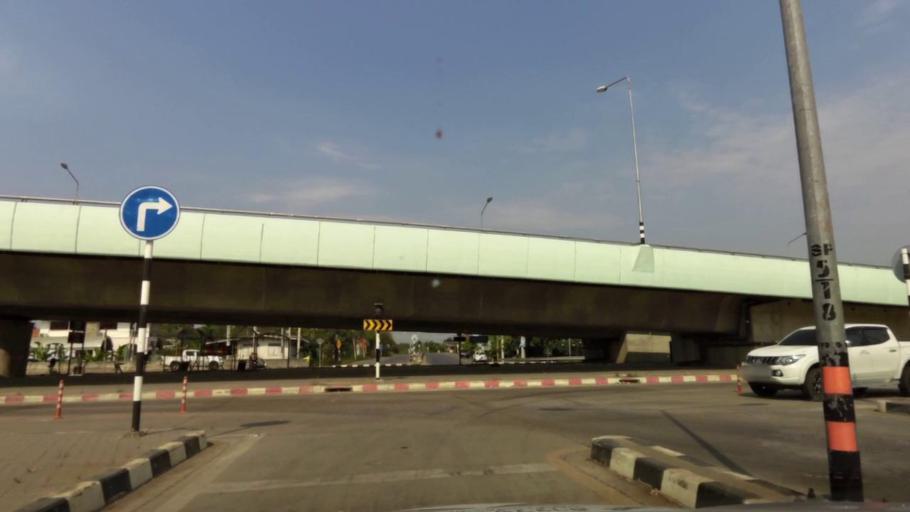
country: TH
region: Phra Nakhon Si Ayutthaya
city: Phra Nakhon Si Ayutthaya
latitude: 14.3307
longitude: 100.5774
